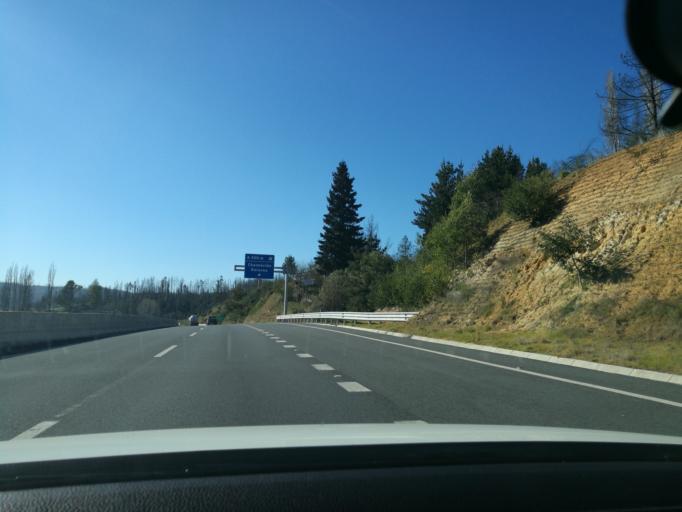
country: CL
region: Biobio
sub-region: Provincia de Concepcion
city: Chiguayante
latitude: -36.8566
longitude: -72.8874
